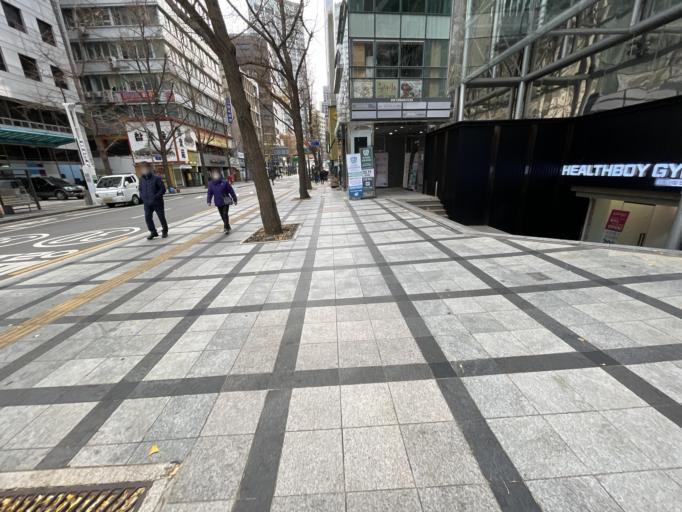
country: KR
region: Seoul
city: Seoul
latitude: 37.5678
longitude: 126.9791
